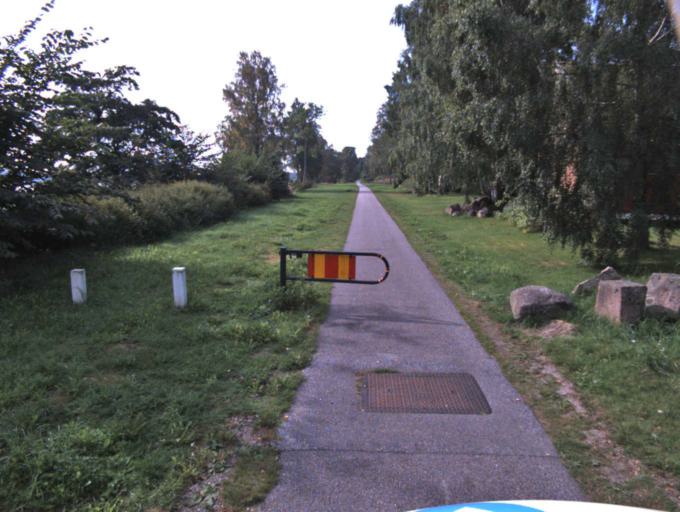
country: SE
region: Vaestra Goetaland
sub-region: Ulricehamns Kommun
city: Ulricehamn
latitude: 57.6767
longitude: 13.3740
